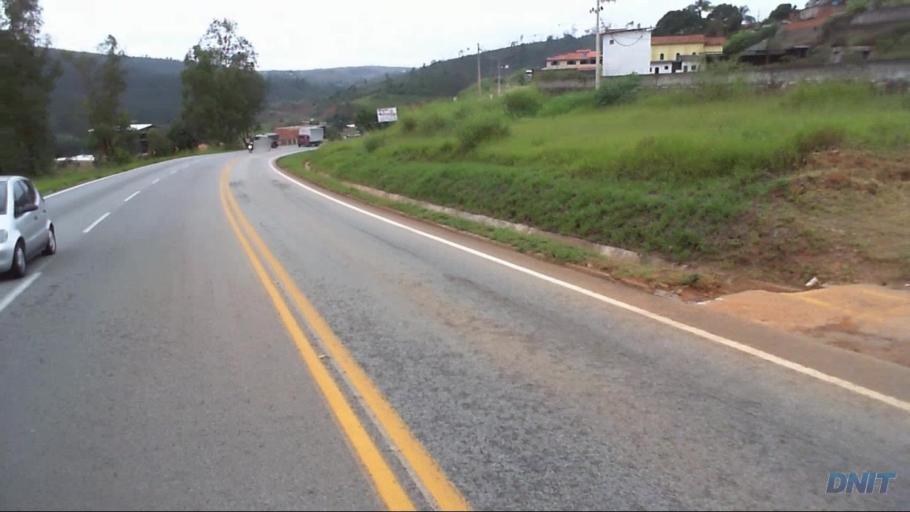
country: BR
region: Minas Gerais
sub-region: Joao Monlevade
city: Joao Monlevade
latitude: -19.8299
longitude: -43.0931
